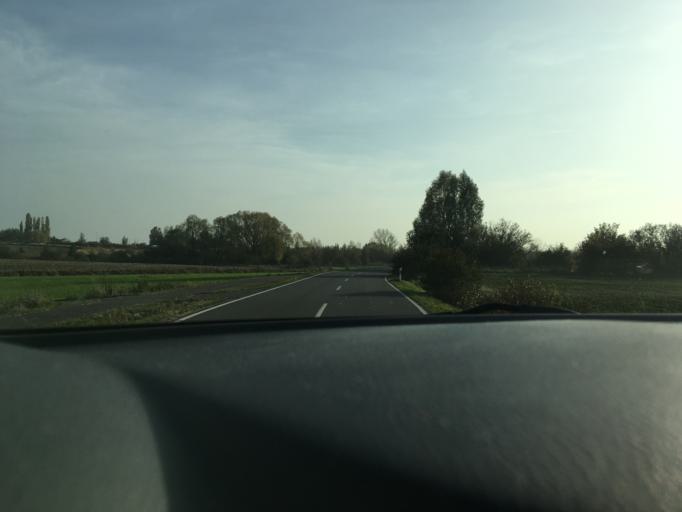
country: DE
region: Saxony
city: Espenhain
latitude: 51.1789
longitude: 12.4549
